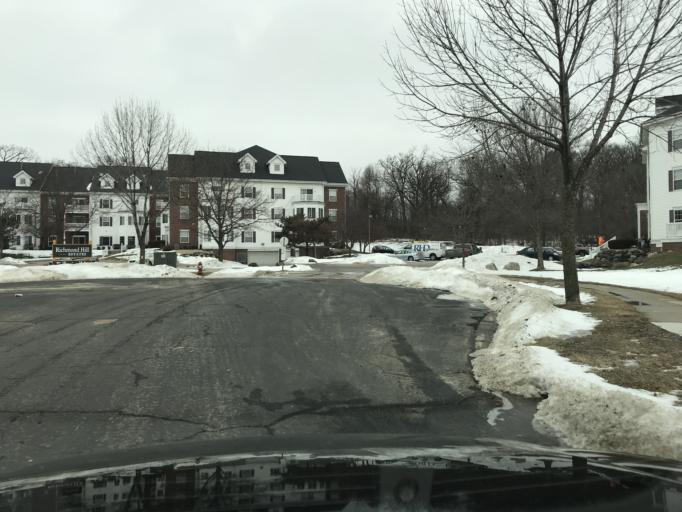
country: US
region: Wisconsin
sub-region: Dane County
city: Monona
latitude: 43.0763
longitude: -89.2783
